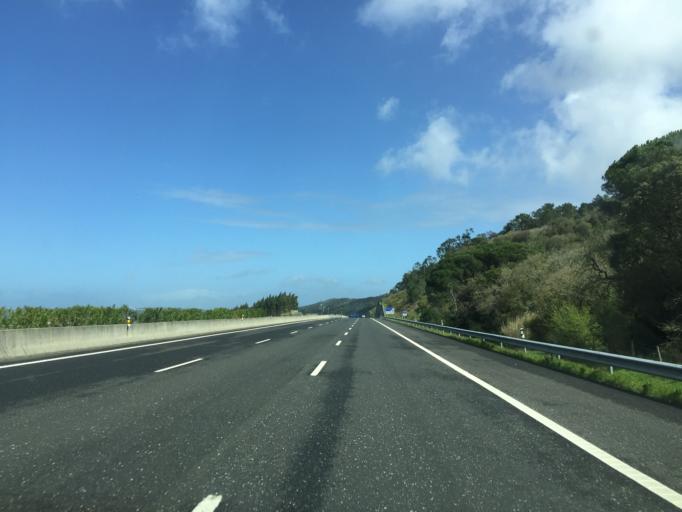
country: PT
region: Leiria
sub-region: Caldas da Rainha
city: Caldas da Rainha
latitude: 39.4844
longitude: -9.0982
